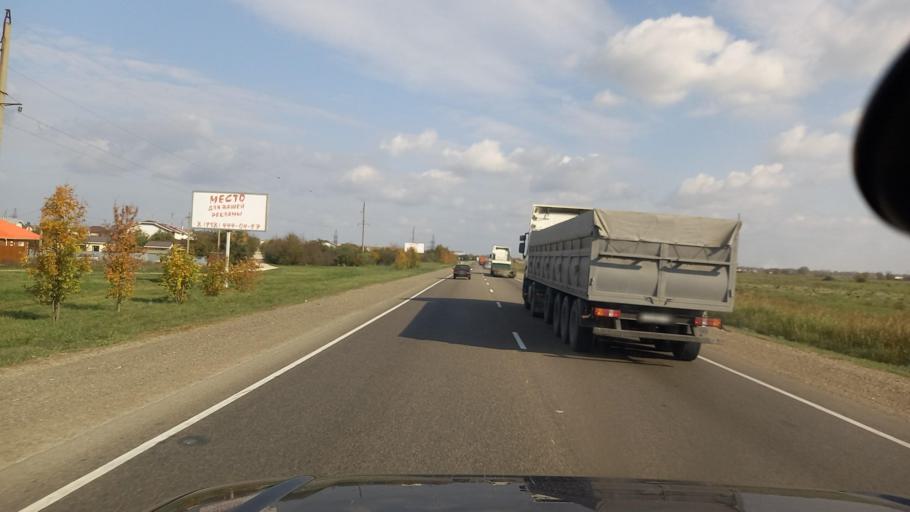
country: RU
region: Krasnodarskiy
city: Abinsk
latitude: 44.8520
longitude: 38.1850
